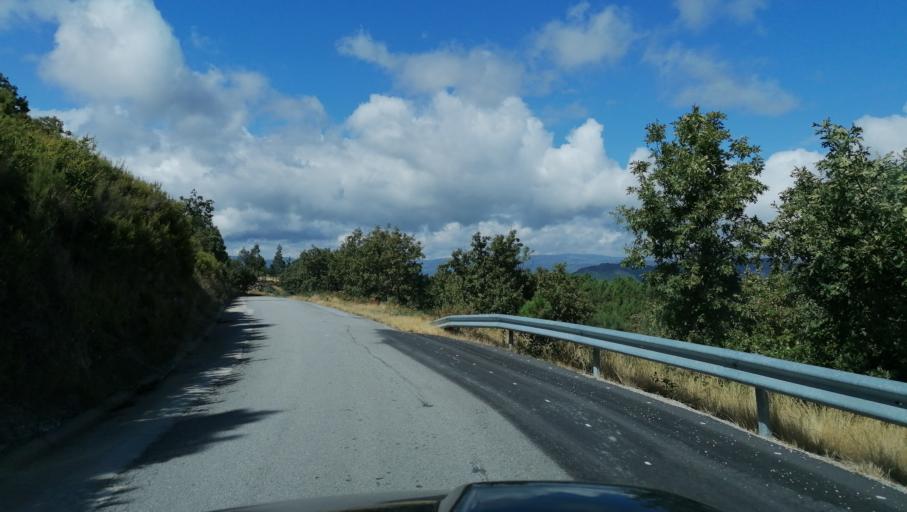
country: PT
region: Vila Real
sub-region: Vila Pouca de Aguiar
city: Vila Pouca de Aguiar
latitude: 41.5602
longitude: -7.6819
